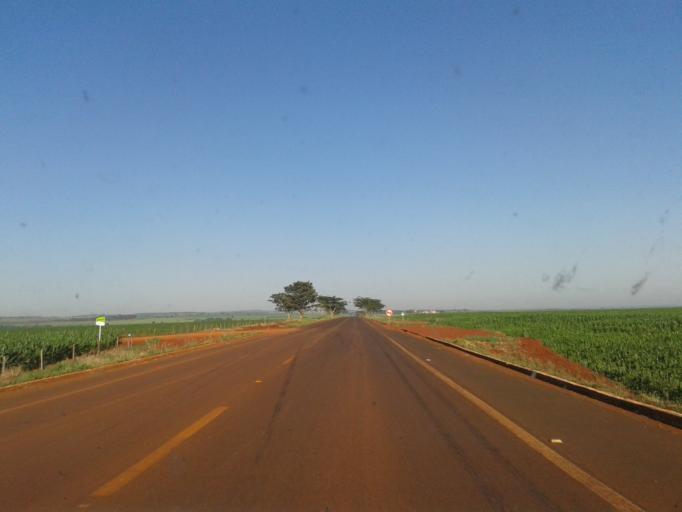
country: BR
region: Minas Gerais
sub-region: Capinopolis
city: Capinopolis
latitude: -18.6985
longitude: -49.6423
